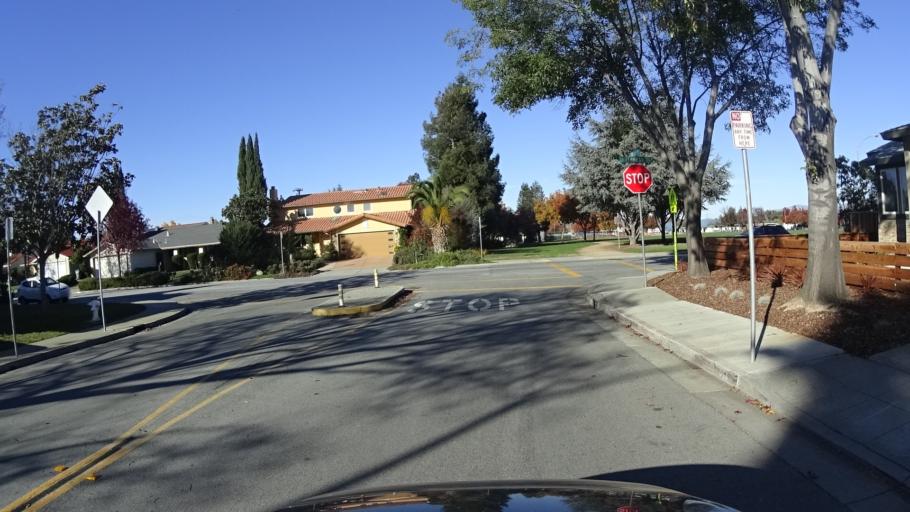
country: US
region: California
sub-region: Santa Clara County
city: Cupertino
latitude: 37.3409
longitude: -122.0278
